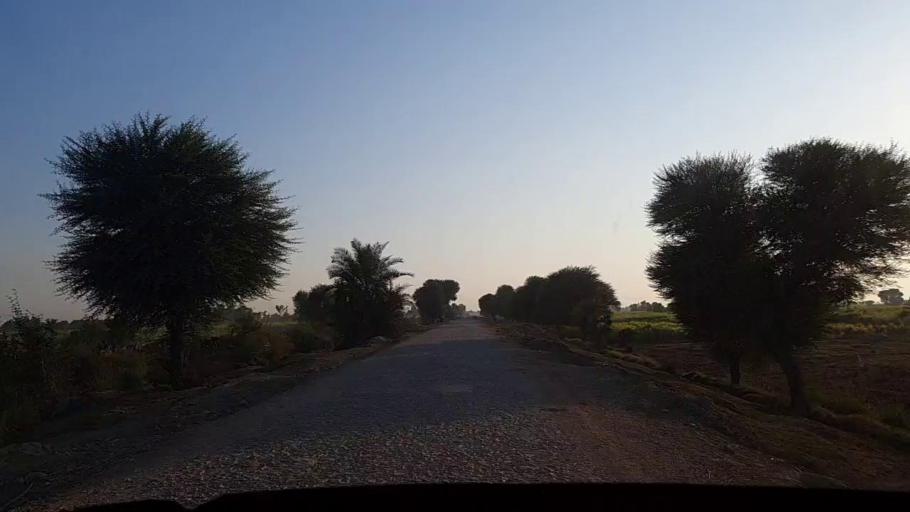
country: PK
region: Sindh
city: Sobhadero
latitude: 27.3756
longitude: 68.3793
